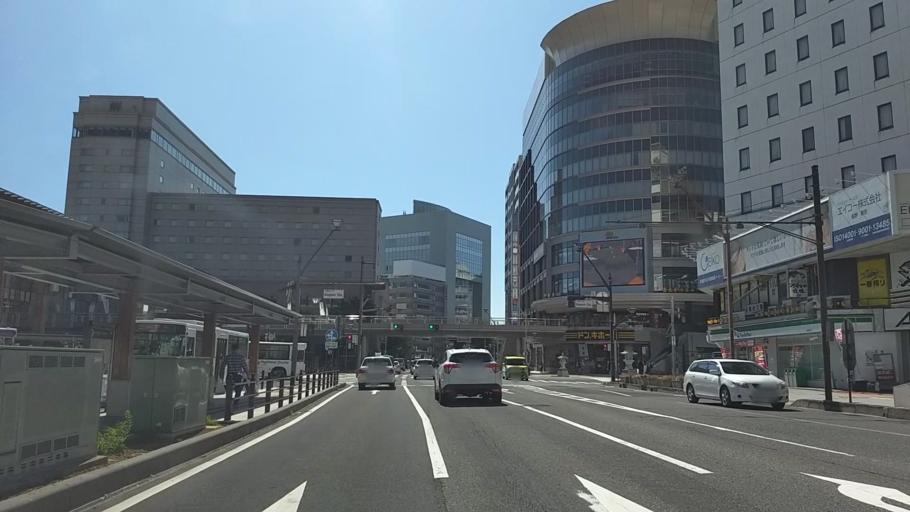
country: JP
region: Nagano
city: Nagano-shi
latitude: 36.6442
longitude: 138.1882
